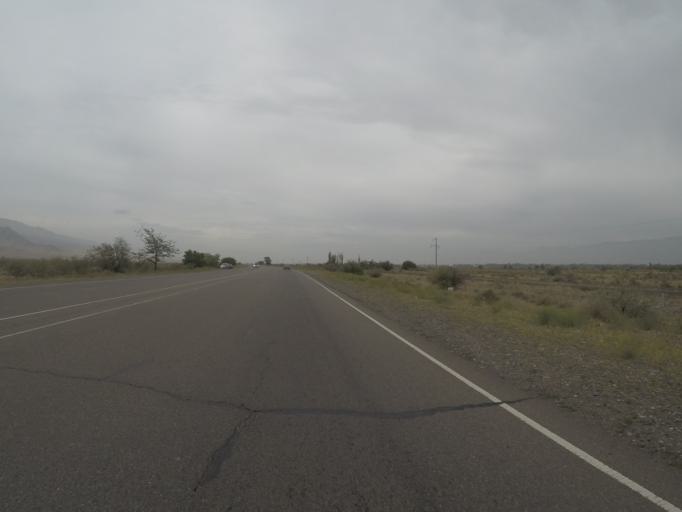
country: KG
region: Chuy
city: Tokmok
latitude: 42.8294
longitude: 75.4727
